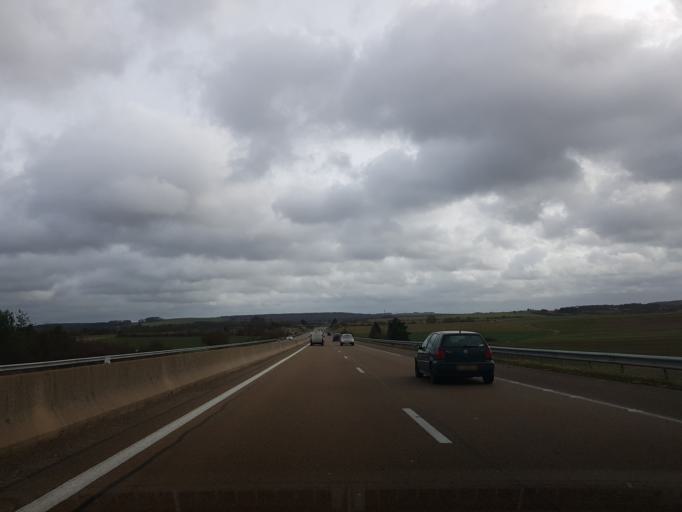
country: FR
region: Champagne-Ardenne
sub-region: Departement de la Haute-Marne
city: Rolampont
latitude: 47.9427
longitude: 5.1898
